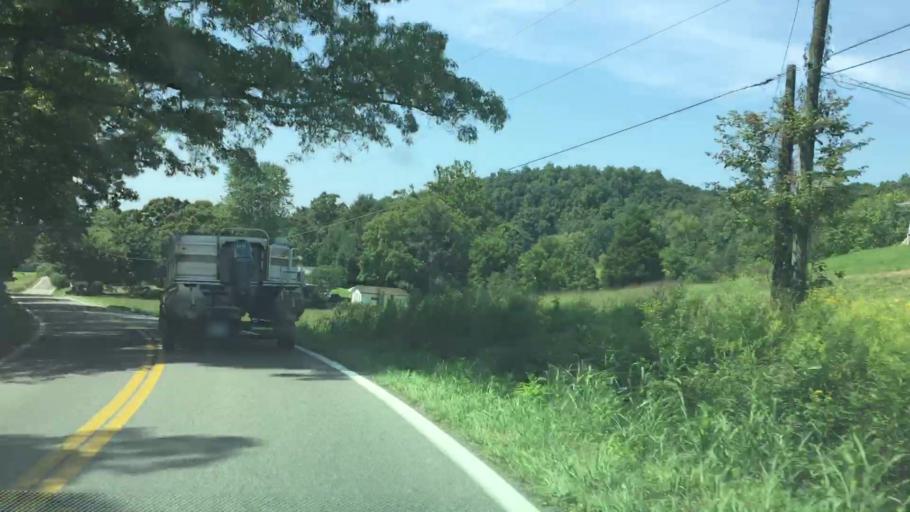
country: US
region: Virginia
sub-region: Washington County
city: Abingdon
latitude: 36.6138
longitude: -82.0232
